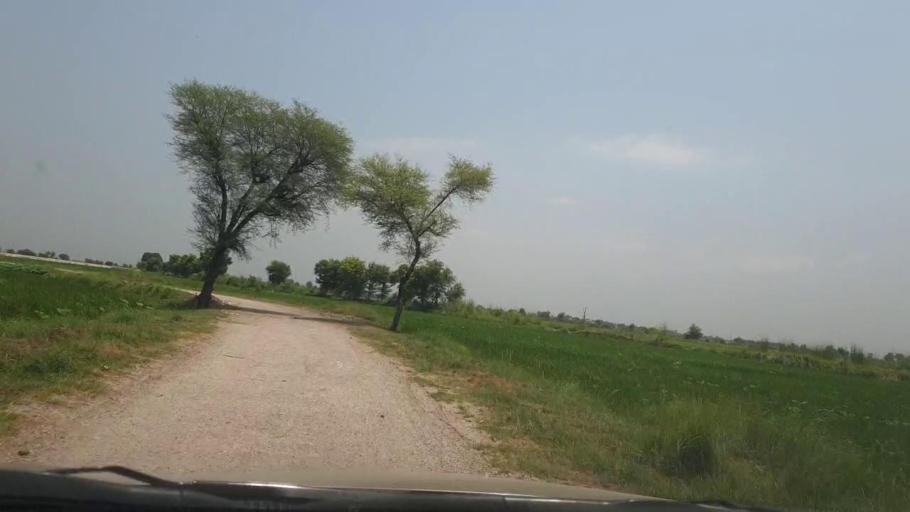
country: PK
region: Sindh
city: Ratodero
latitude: 27.7354
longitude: 68.3182
